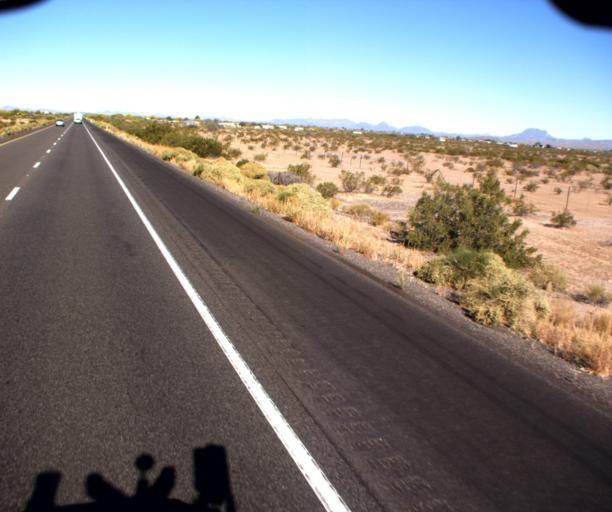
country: US
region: Arizona
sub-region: Maricopa County
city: Gila Bend
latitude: 32.9295
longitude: -112.6896
